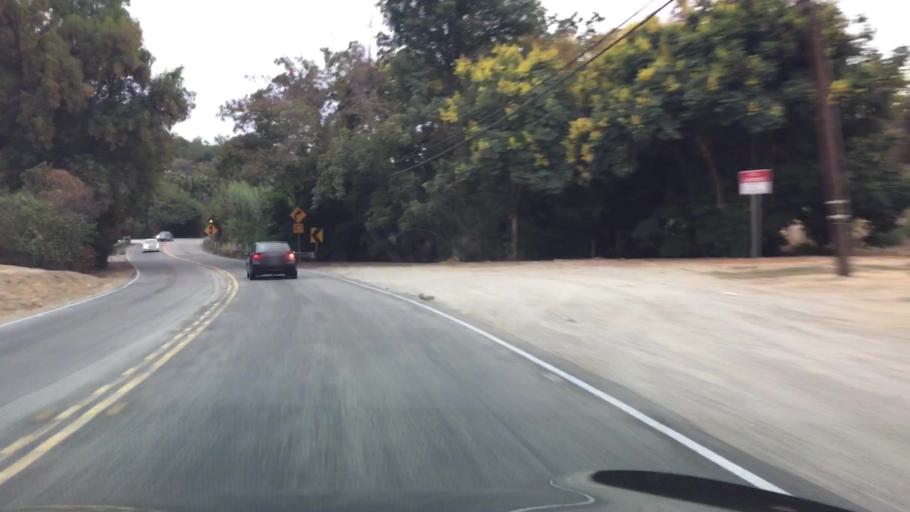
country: US
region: California
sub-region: Los Angeles County
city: La Habra Heights
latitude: 33.9553
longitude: -117.9586
